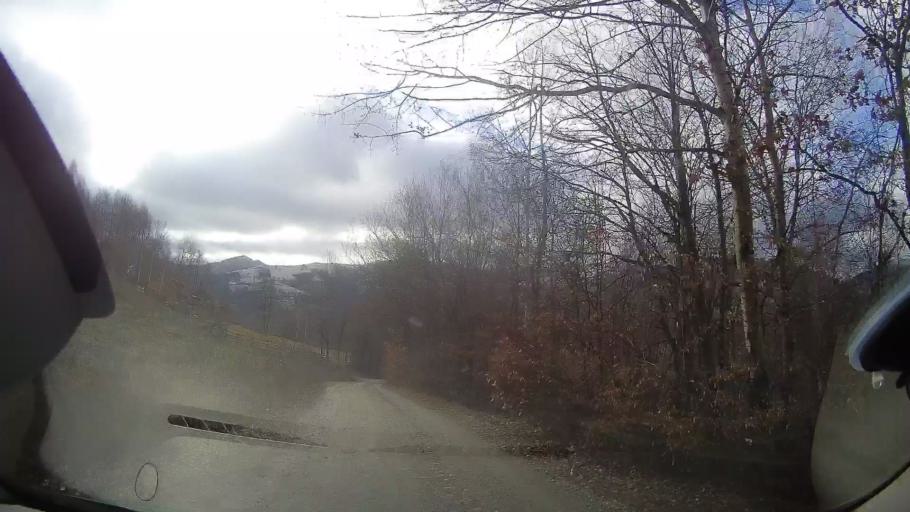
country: RO
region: Cluj
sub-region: Comuna Valea Ierii
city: Valea Ierii
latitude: 46.6823
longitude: 23.3109
